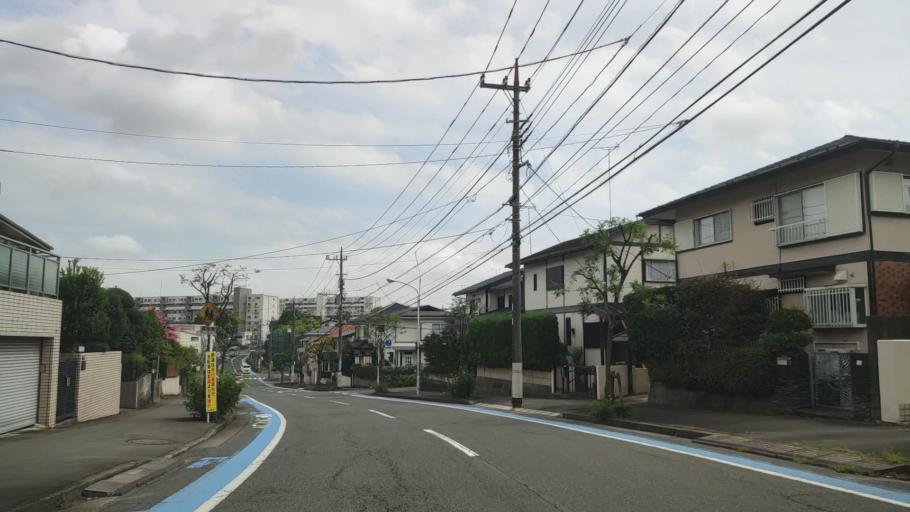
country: JP
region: Tokyo
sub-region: Machida-shi
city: Machida
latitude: 35.5125
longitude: 139.4547
